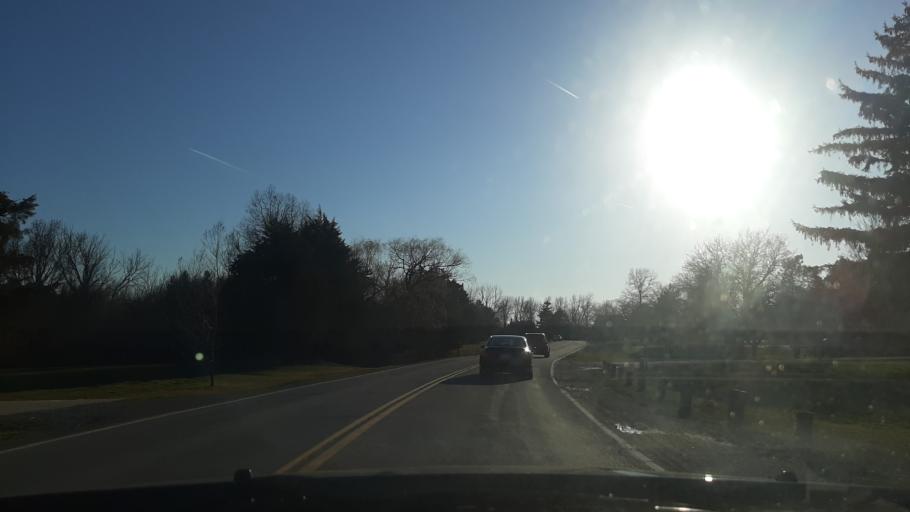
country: US
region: New York
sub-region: Niagara County
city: Lewiston
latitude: 43.1698
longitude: -79.0583
